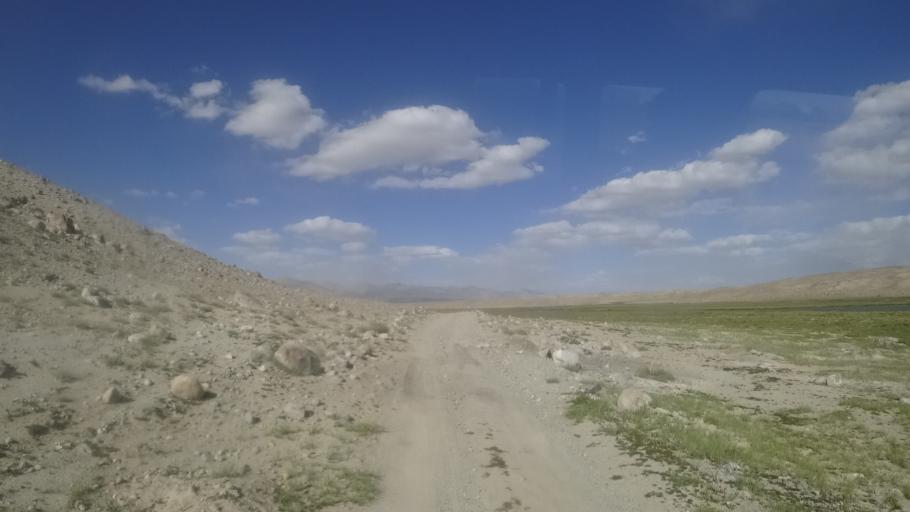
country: AF
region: Badakhshan
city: Khandud
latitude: 37.4121
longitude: 73.2228
